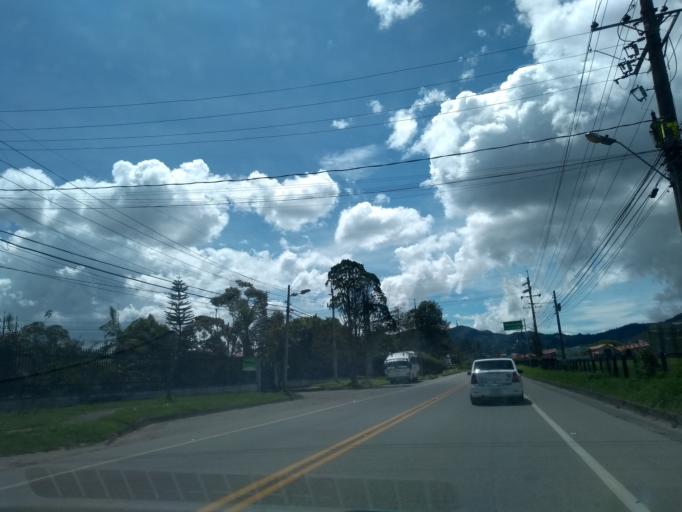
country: CO
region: Antioquia
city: La Ceja
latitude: 6.0389
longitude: -75.4178
